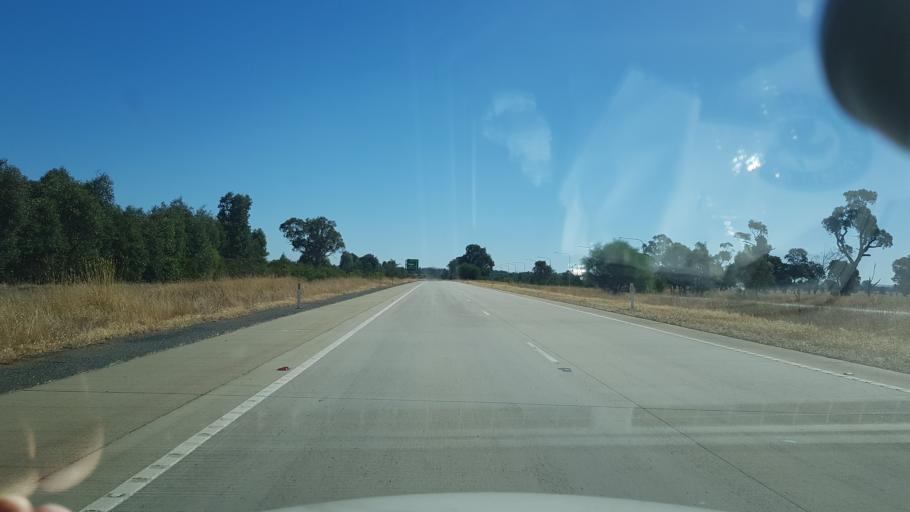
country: AU
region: New South Wales
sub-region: Greater Hume Shire
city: Jindera
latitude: -35.9250
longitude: 147.0188
